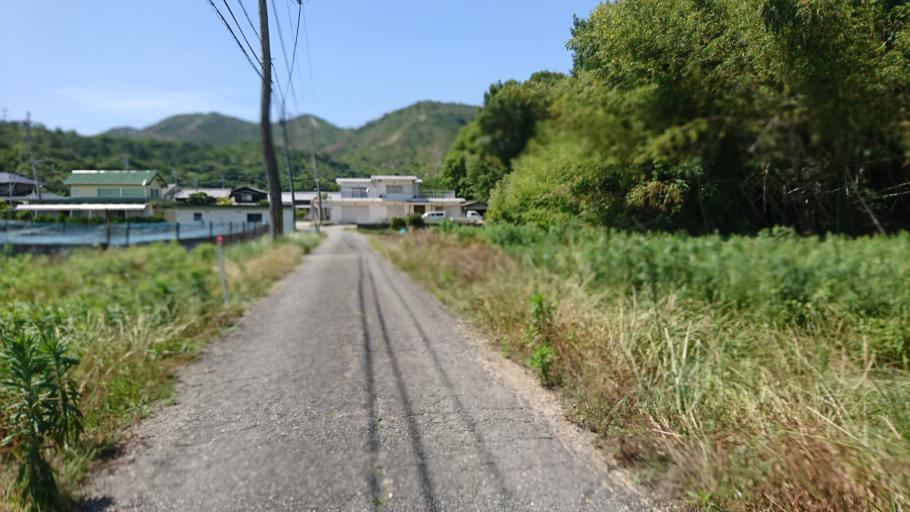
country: JP
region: Hyogo
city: Kakogawacho-honmachi
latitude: 34.8080
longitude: 134.7864
